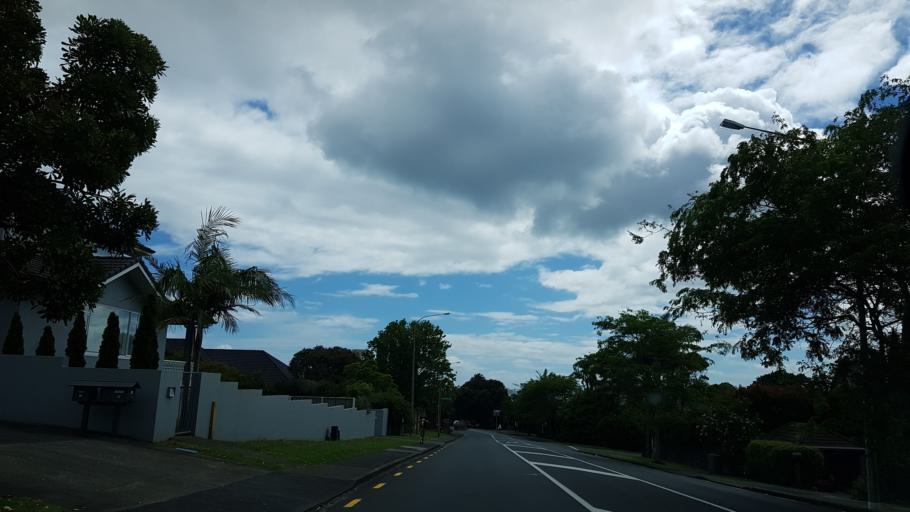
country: NZ
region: Auckland
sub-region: Auckland
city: North Shore
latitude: -36.7850
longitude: 174.7704
